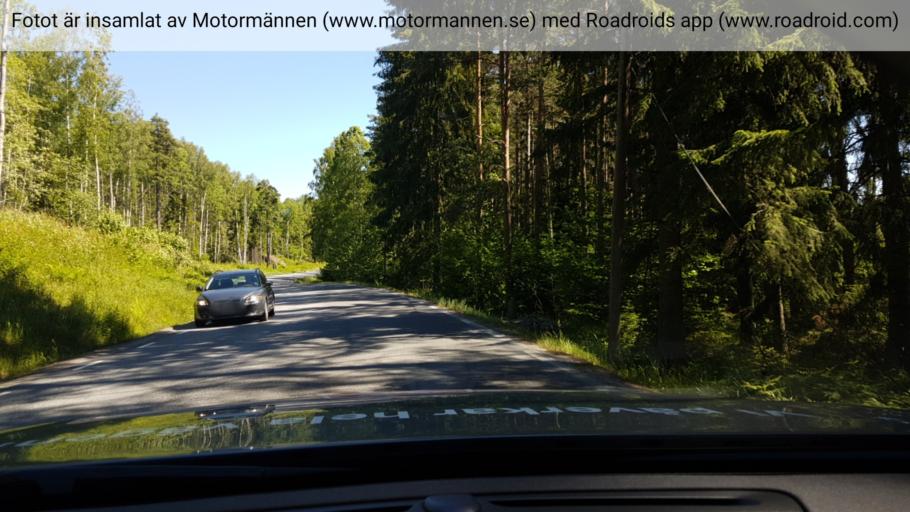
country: SE
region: Stockholm
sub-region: Haninge Kommun
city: Haninge
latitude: 59.1639
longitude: 18.1712
